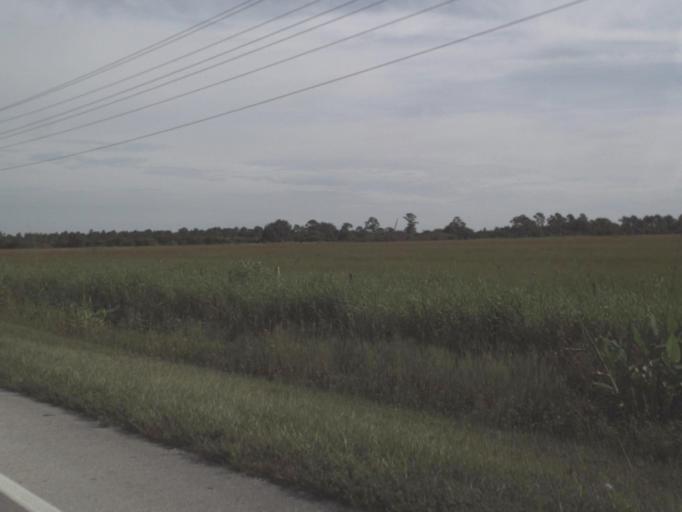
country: US
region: Florida
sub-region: Lee County
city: Fort Myers Shores
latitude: 26.7661
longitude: -81.7608
